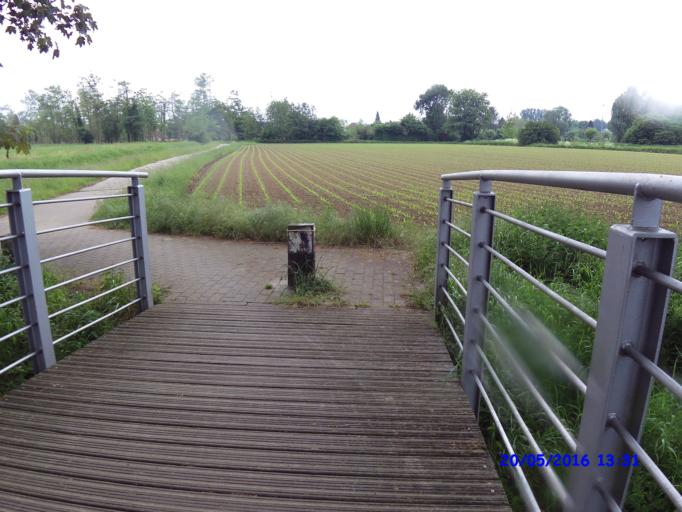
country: BE
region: Flanders
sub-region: Provincie Vlaams-Brabant
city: Rotselaar
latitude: 50.9284
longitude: 4.7114
